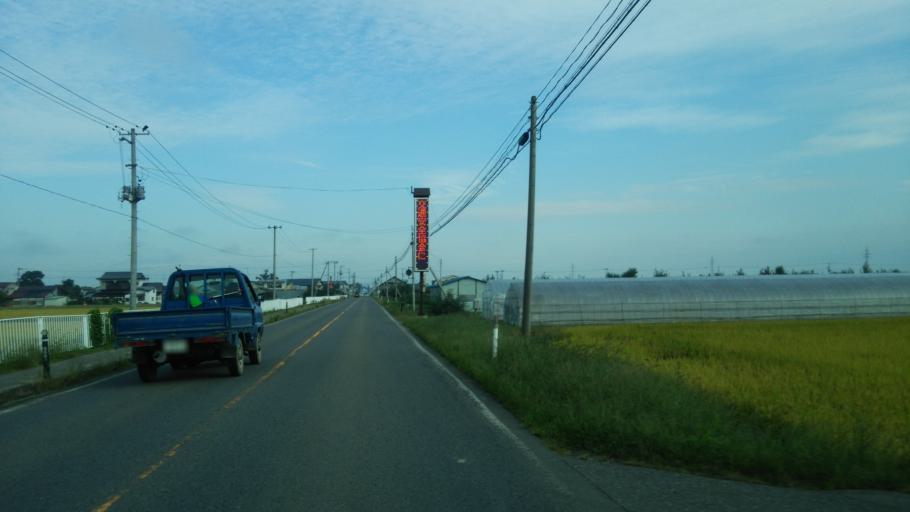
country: JP
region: Fukushima
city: Kitakata
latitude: 37.5010
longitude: 139.8705
